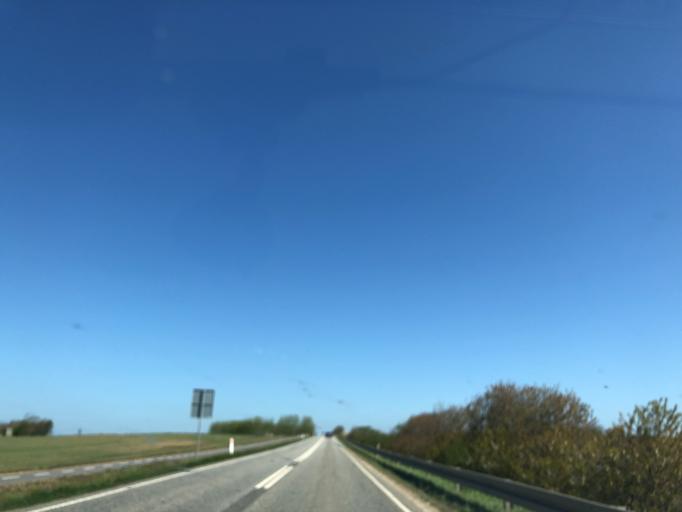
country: DK
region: Central Jutland
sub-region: Holstebro Kommune
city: Holstebro
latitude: 56.3886
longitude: 8.6574
